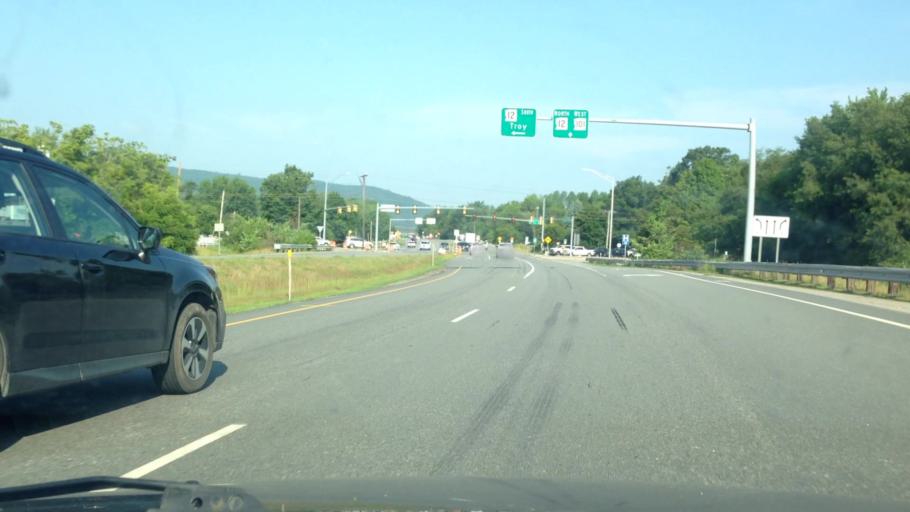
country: US
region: New Hampshire
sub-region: Cheshire County
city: Keene
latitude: 42.9213
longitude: -72.2739
